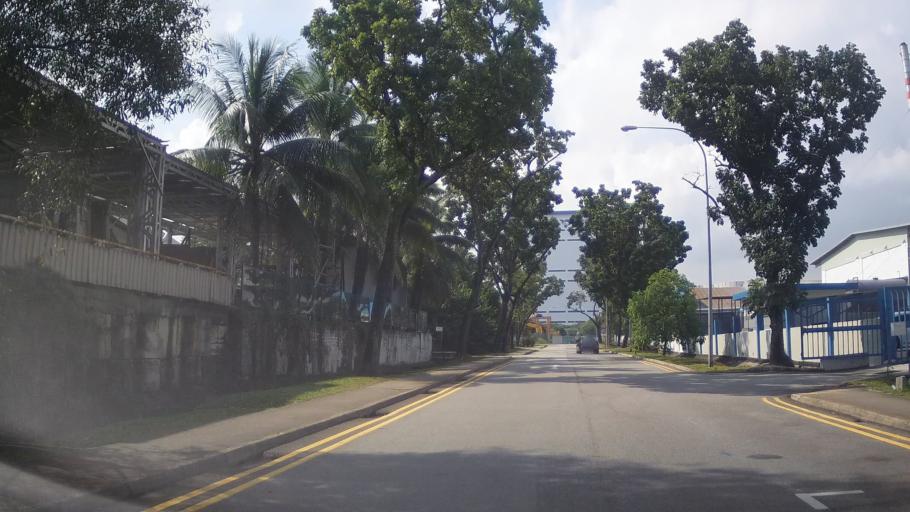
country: MY
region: Johor
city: Johor Bahru
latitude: 1.3263
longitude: 103.6993
